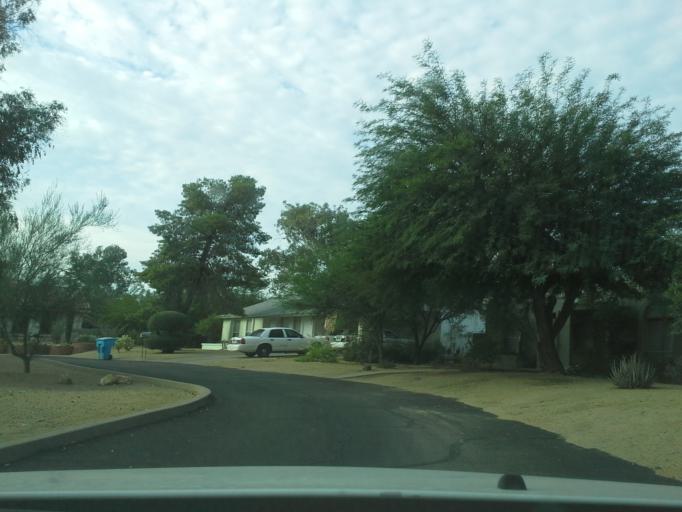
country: US
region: Arizona
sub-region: Maricopa County
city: Paradise Valley
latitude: 33.6106
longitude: -112.0604
